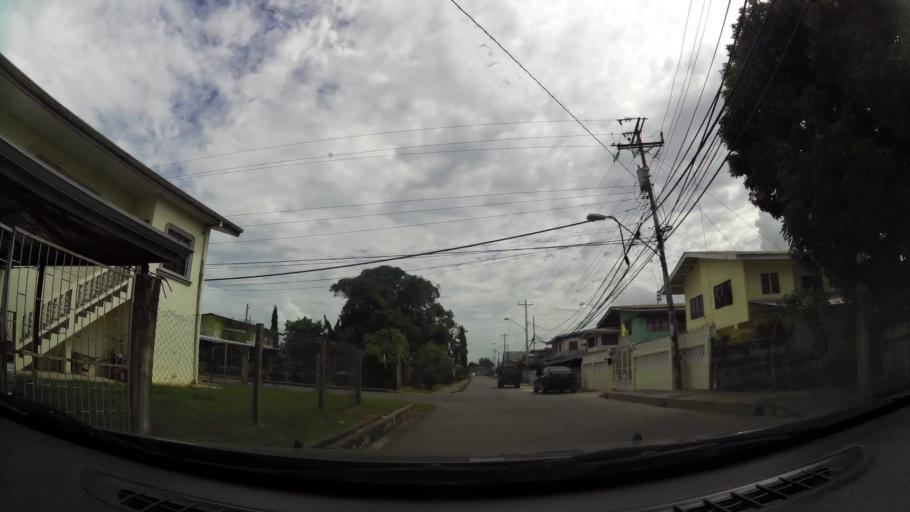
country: TT
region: Couva-Tabaquite-Talparo
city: Couva
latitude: 10.4009
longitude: -61.4706
